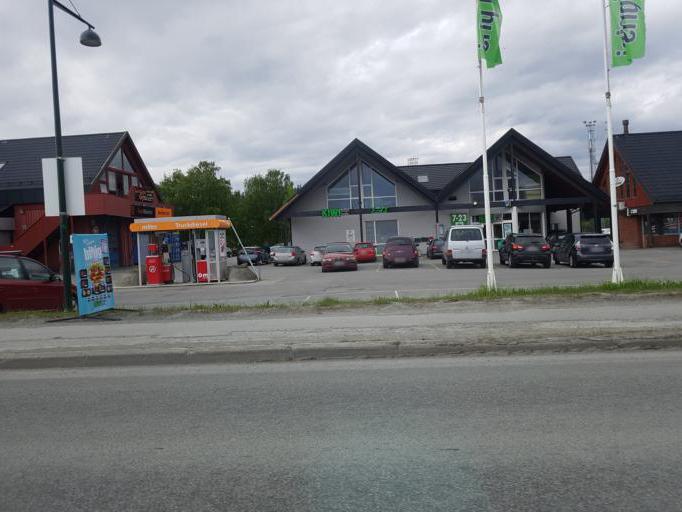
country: NO
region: Nord-Trondelag
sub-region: Levanger
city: Levanger
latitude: 63.7400
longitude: 11.2837
